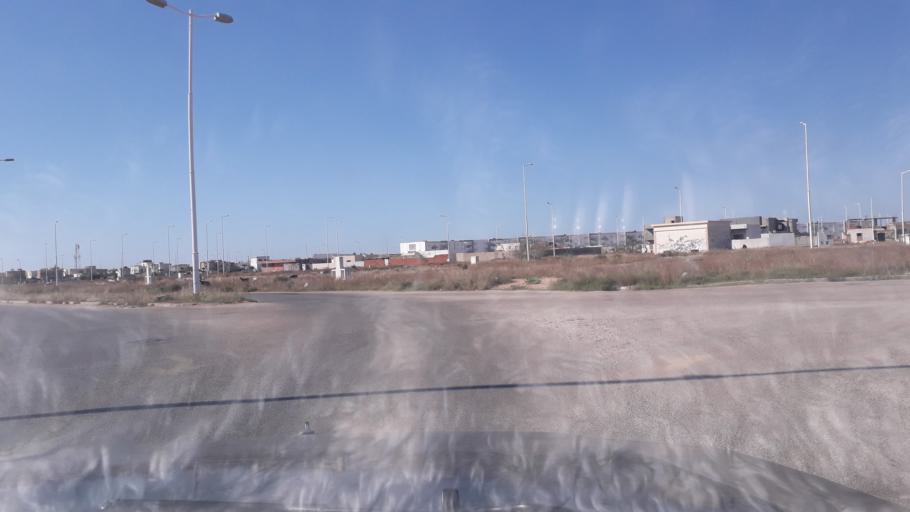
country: TN
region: Safaqis
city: Al Qarmadah
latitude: 34.8344
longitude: 10.7539
